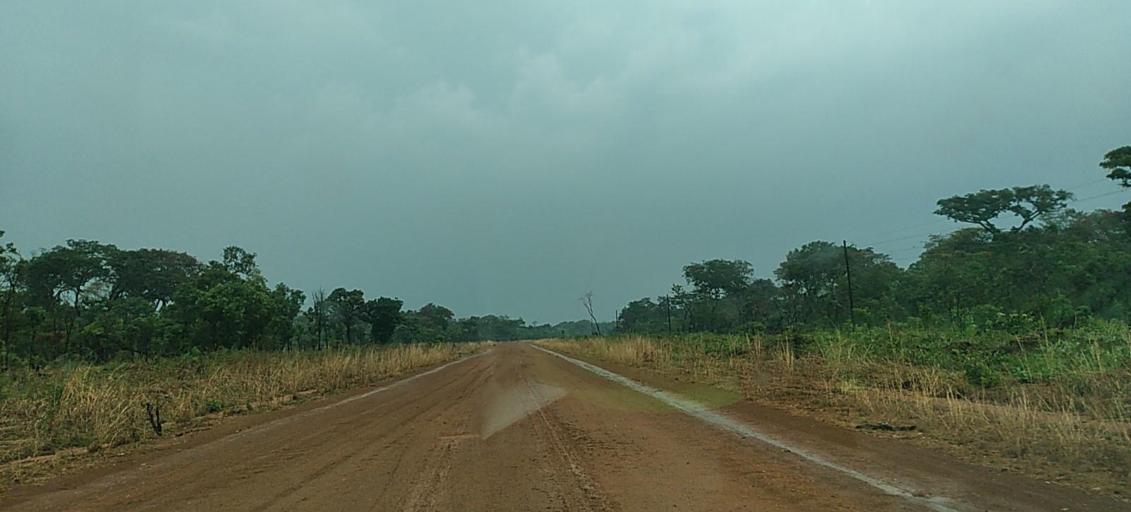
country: ZM
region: North-Western
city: Mwinilunga
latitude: -11.6142
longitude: 24.3998
